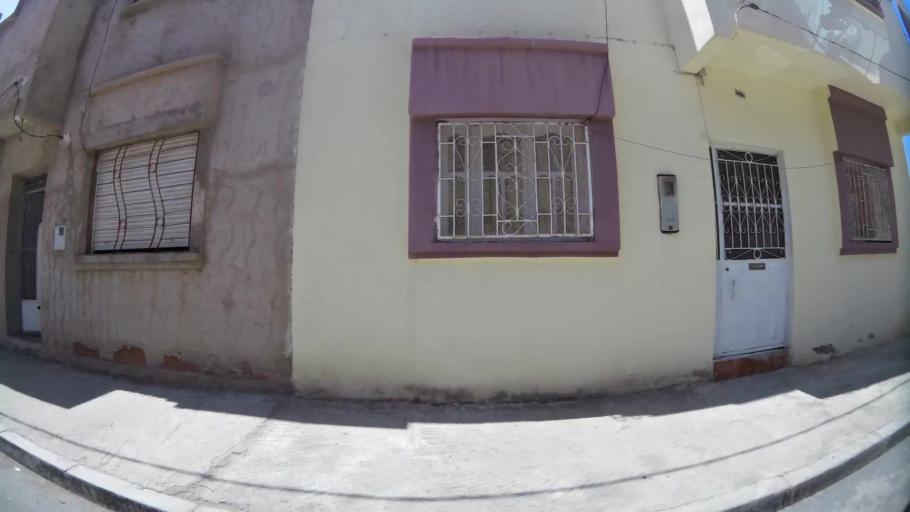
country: MA
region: Oriental
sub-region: Oujda-Angad
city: Oujda
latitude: 34.6853
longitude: -1.8993
